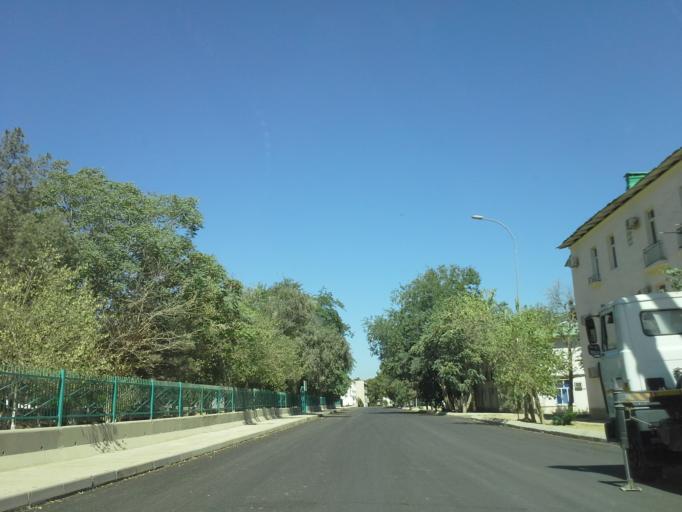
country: TM
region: Ahal
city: Ashgabat
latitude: 37.9456
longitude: 58.3520
